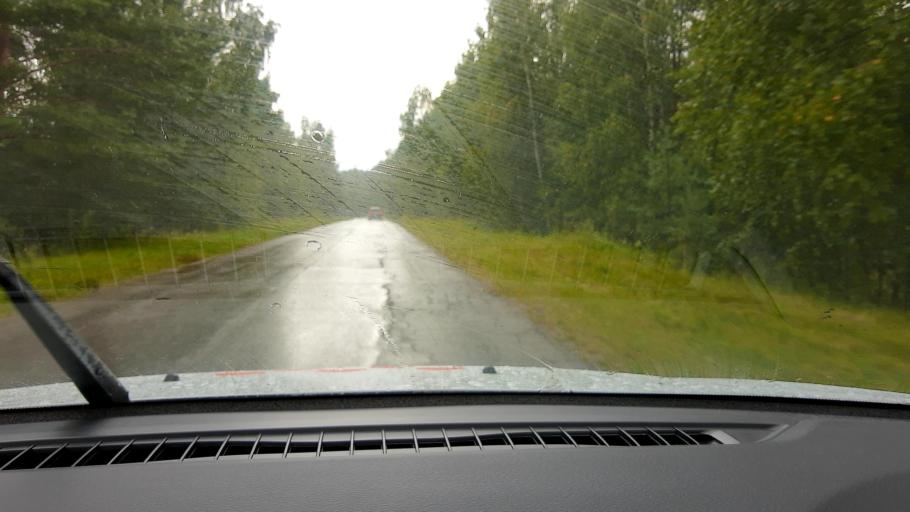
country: RU
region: Nizjnij Novgorod
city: Dal'neye Konstantinovo
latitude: 55.9518
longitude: 43.9600
